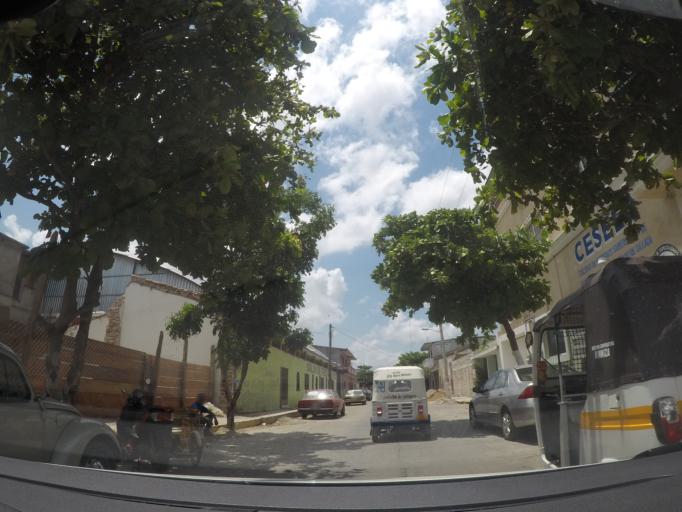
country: MX
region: Oaxaca
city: Juchitan de Zaragoza
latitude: 16.4388
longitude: -95.0232
